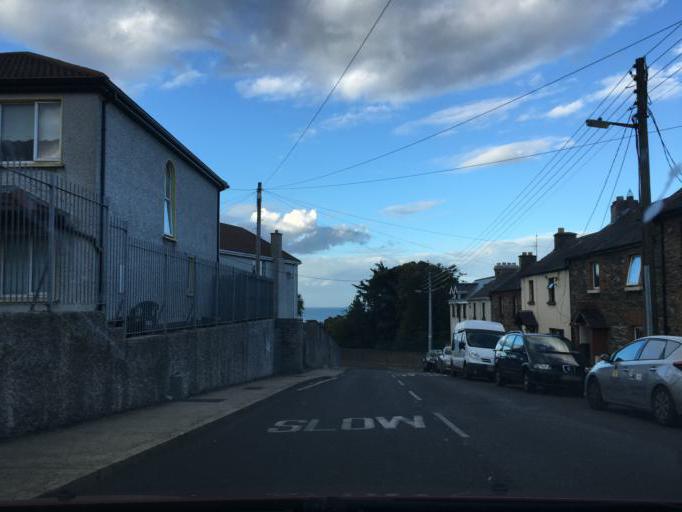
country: IE
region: Leinster
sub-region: Wicklow
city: Wicklow
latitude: 52.9763
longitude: -6.0412
